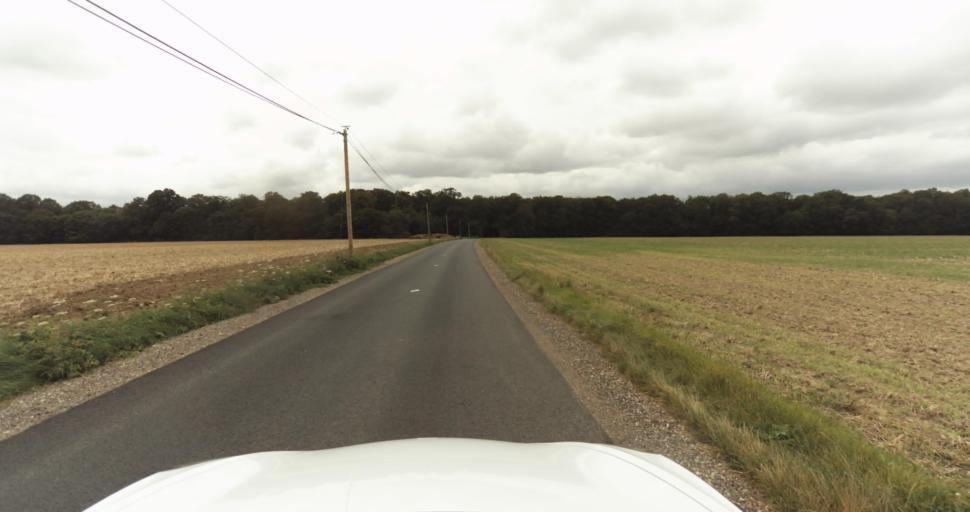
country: FR
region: Haute-Normandie
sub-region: Departement de l'Eure
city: Damville
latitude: 48.9284
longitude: 1.0813
